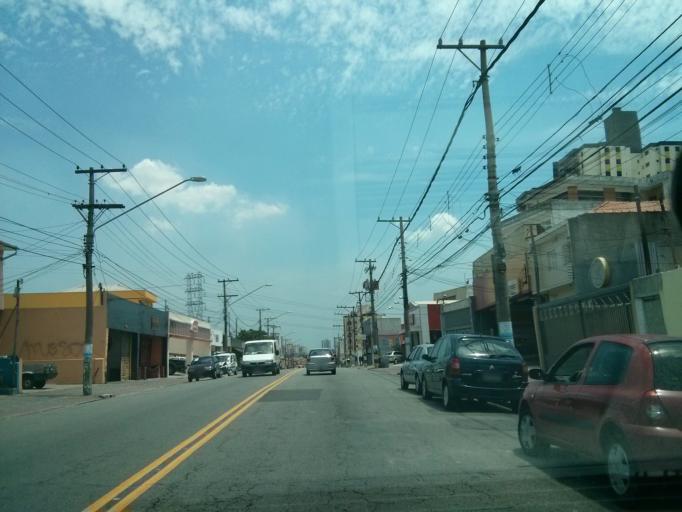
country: BR
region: Sao Paulo
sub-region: Sao Paulo
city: Sao Paulo
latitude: -23.6093
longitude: -46.6174
